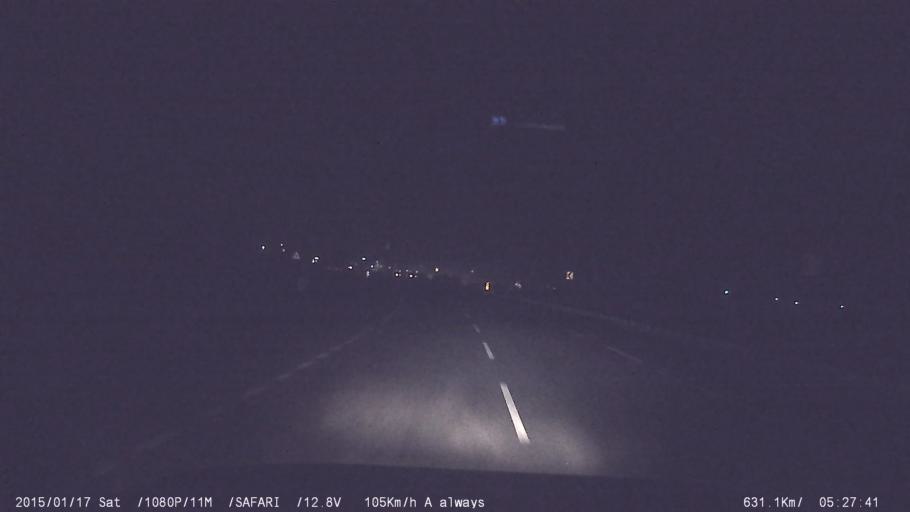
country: IN
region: Tamil Nadu
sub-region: Vellore
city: Arcot
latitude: 12.9297
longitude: 79.2623
